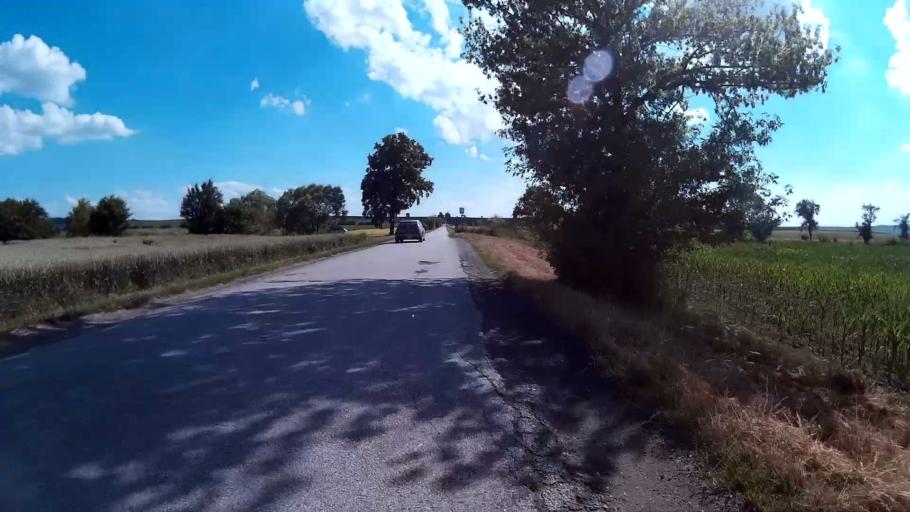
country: CZ
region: South Moravian
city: Krepice
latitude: 49.0269
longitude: 16.7145
